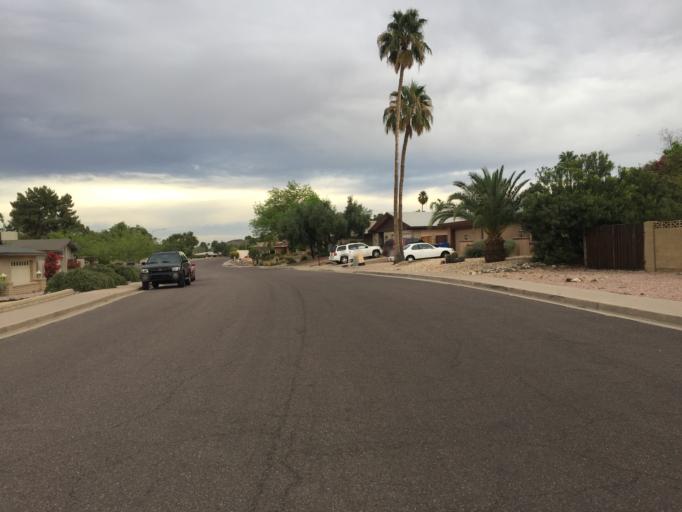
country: US
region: Arizona
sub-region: Maricopa County
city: Paradise Valley
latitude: 33.5707
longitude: -112.0175
